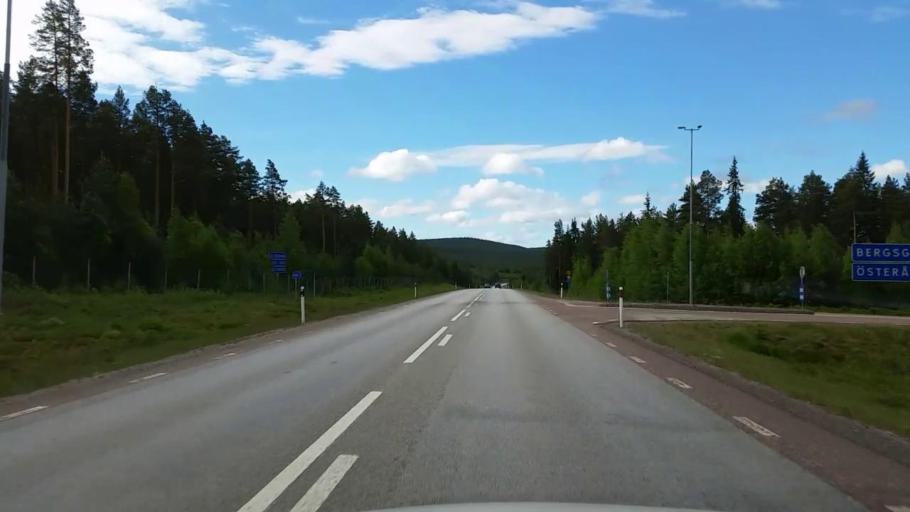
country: SE
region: Dalarna
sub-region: Faluns Kommun
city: Falun
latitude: 60.6674
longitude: 15.6466
